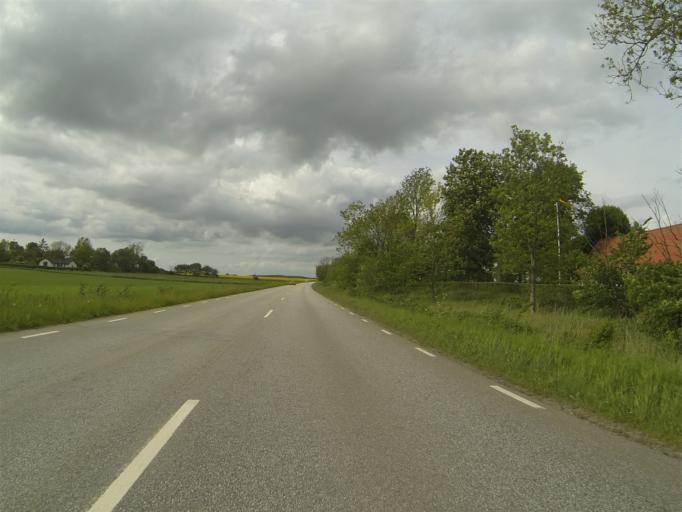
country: SE
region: Skane
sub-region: Lunds Kommun
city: Lund
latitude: 55.6982
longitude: 13.3064
